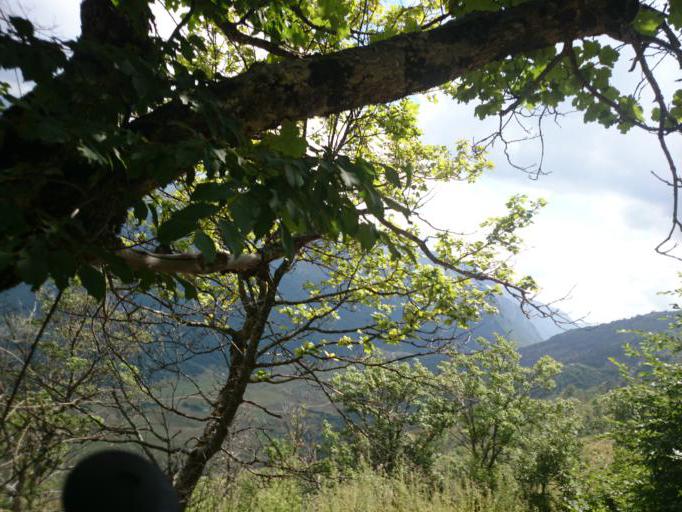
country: AL
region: Lezhe
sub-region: Rrethi i Mirdites
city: Orosh
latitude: 41.8430
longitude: 20.1555
